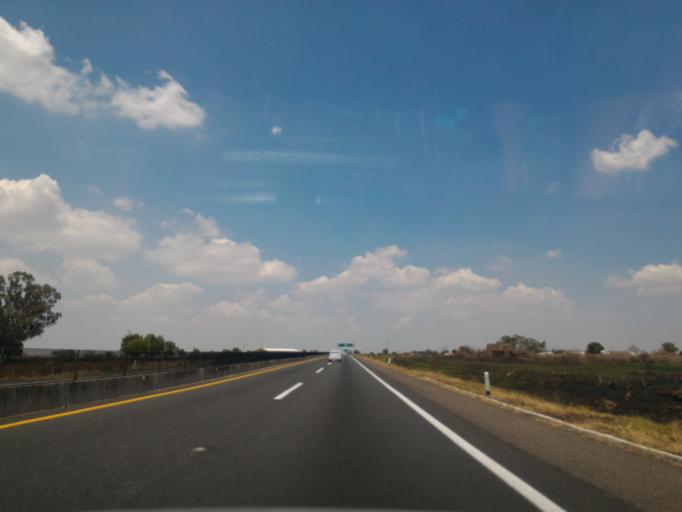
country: MX
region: Jalisco
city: Tepatitlan de Morelos
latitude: 20.8841
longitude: -102.7268
